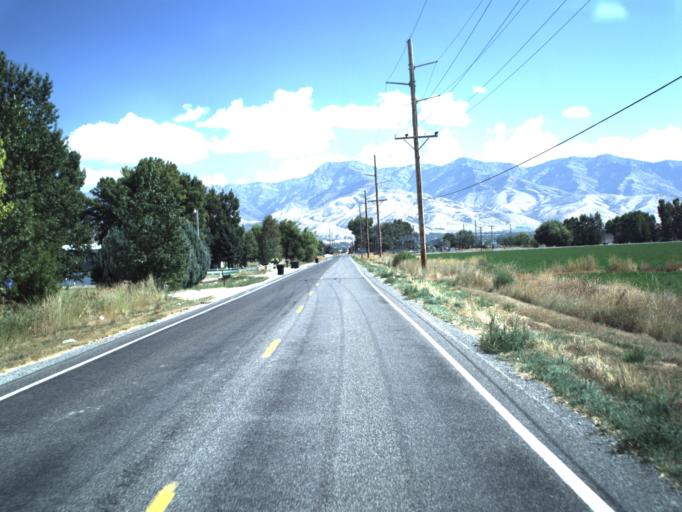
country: US
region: Utah
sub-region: Cache County
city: Benson
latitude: 41.8452
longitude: -111.8987
